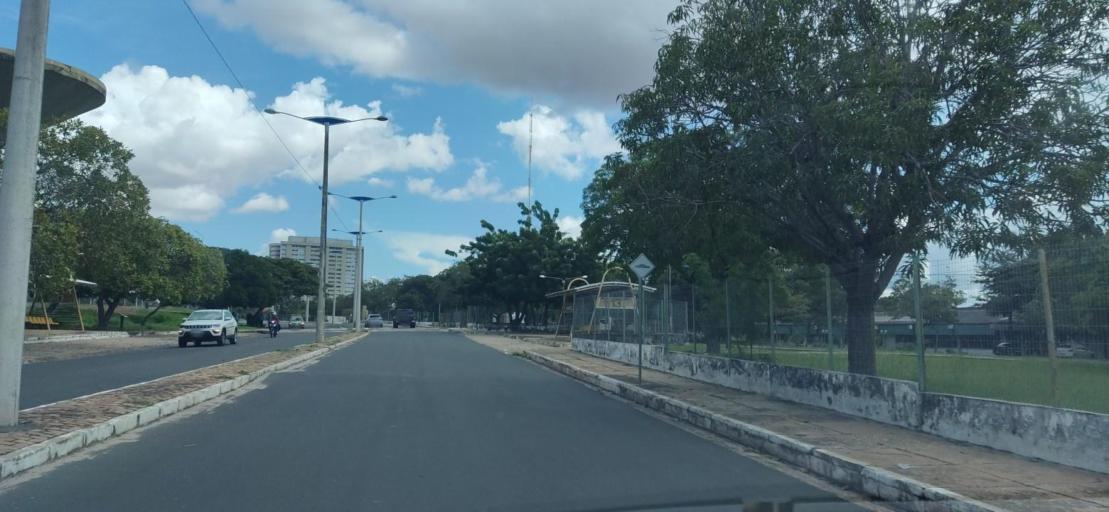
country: BR
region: Piaui
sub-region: Teresina
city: Teresina
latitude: -5.0583
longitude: -42.7950
